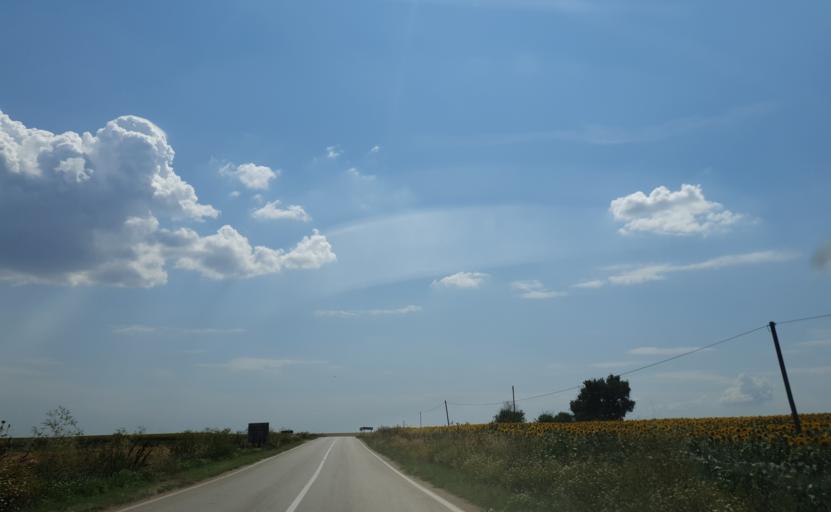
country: TR
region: Tekirdag
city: Beyazkoy
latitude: 41.4544
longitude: 27.6404
